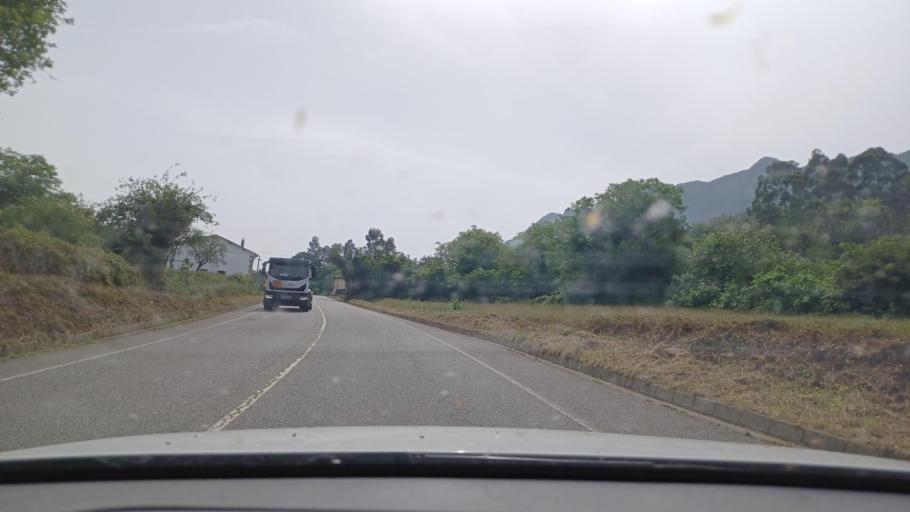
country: ES
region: Asturias
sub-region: Province of Asturias
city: Ribadesella
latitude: 43.4413
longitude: -4.9952
